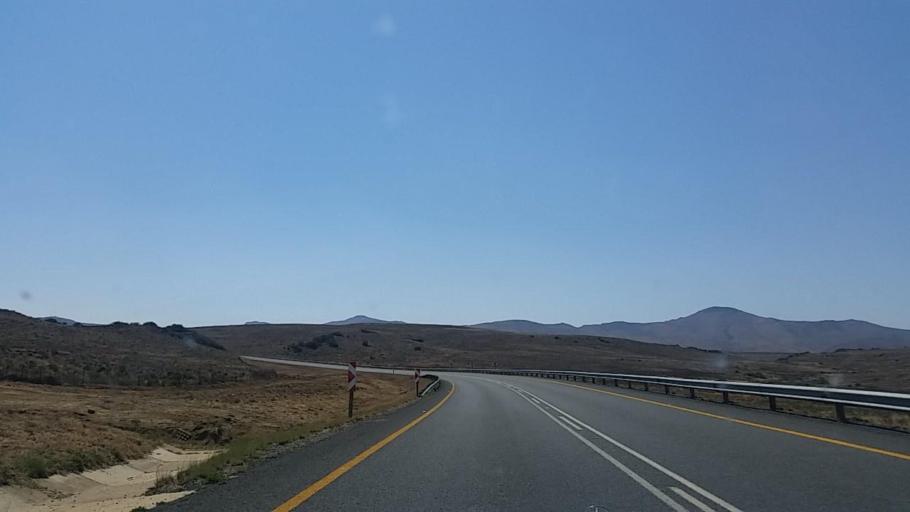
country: ZA
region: Eastern Cape
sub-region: Chris Hani District Municipality
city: Middelburg
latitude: -31.8827
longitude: 24.8186
